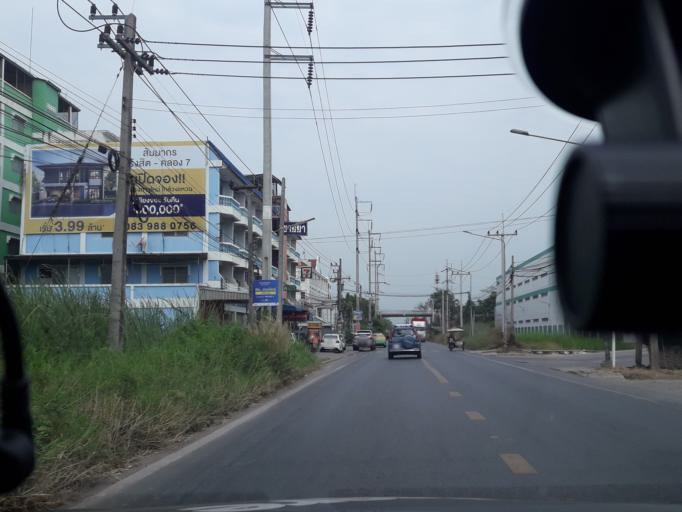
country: TH
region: Pathum Thani
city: Ban Rangsit
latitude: 14.0148
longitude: 100.7532
